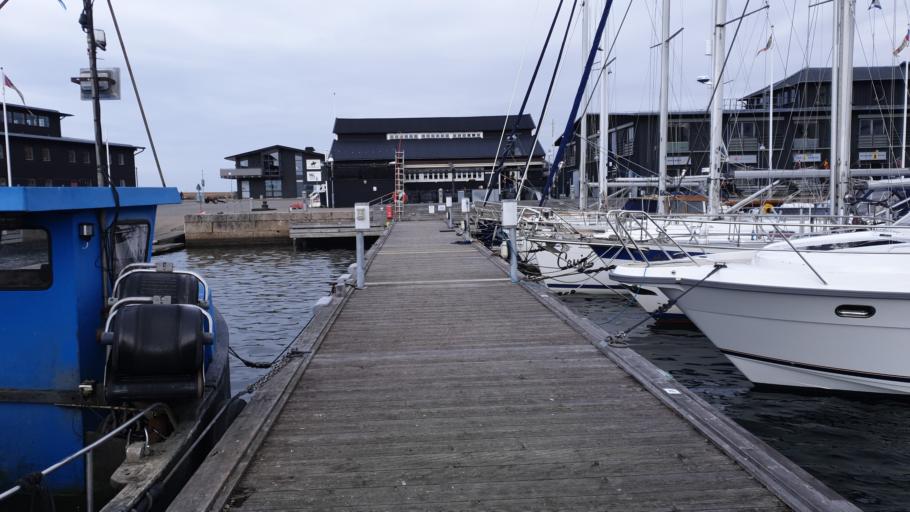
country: SE
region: Skane
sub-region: Helsingborg
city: Helsingborg
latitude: 56.0501
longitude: 12.6851
